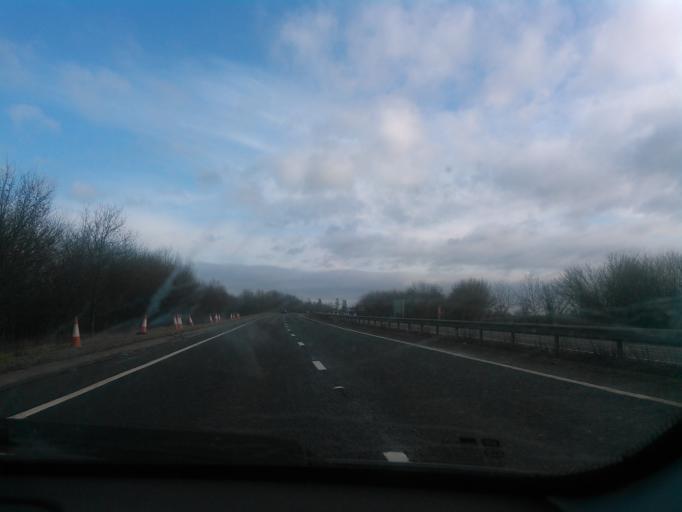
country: GB
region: England
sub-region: Derbyshire
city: Rodsley
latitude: 52.8850
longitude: -1.7384
